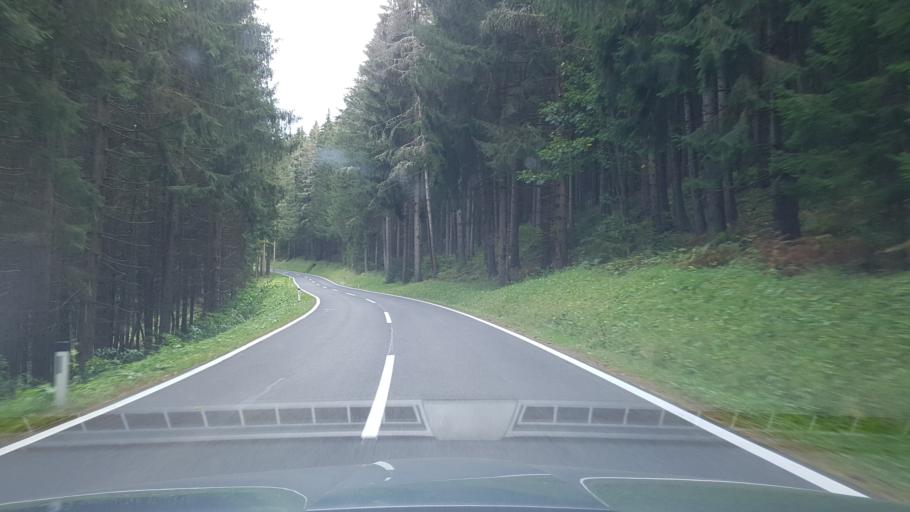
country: AT
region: Styria
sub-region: Politischer Bezirk Murtal
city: Kleinlobming
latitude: 47.1504
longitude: 14.8027
